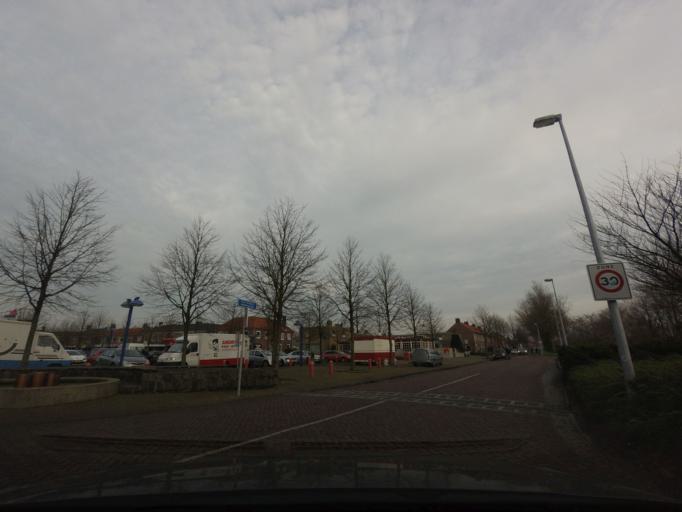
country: NL
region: North Holland
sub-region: Gemeente Hollands Kroon
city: Den Oever
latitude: 52.8509
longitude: 5.0226
